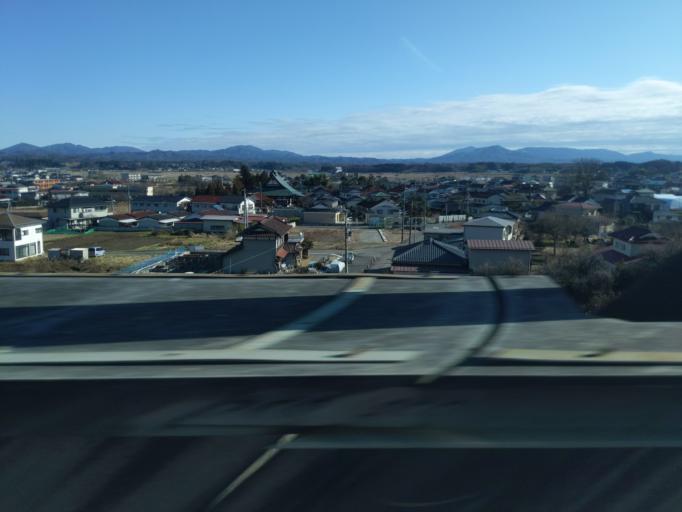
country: JP
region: Fukushima
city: Koriyama
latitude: 37.3542
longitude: 140.3731
